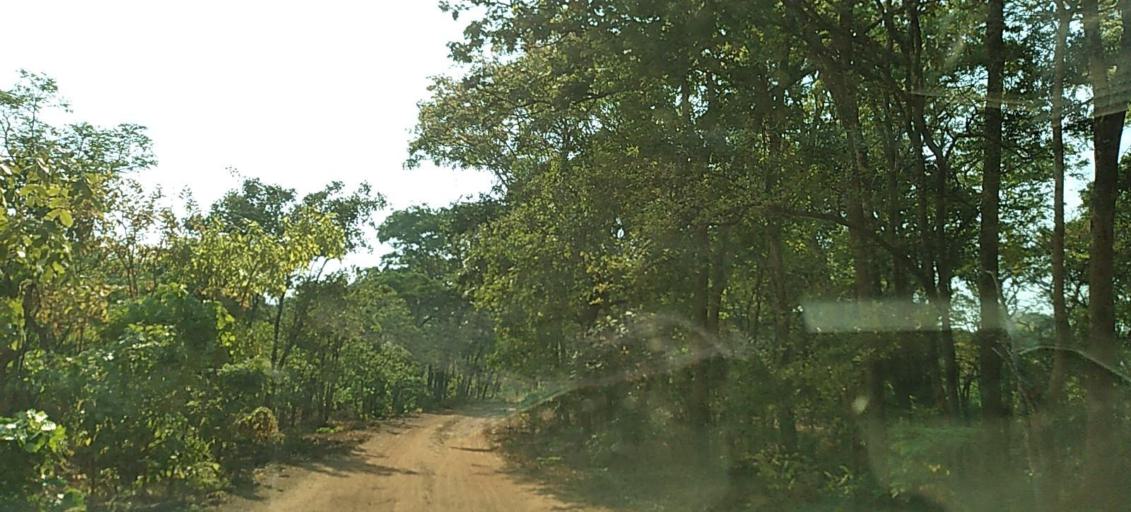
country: ZM
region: Copperbelt
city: Kalulushi
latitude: -13.0066
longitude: 27.7370
